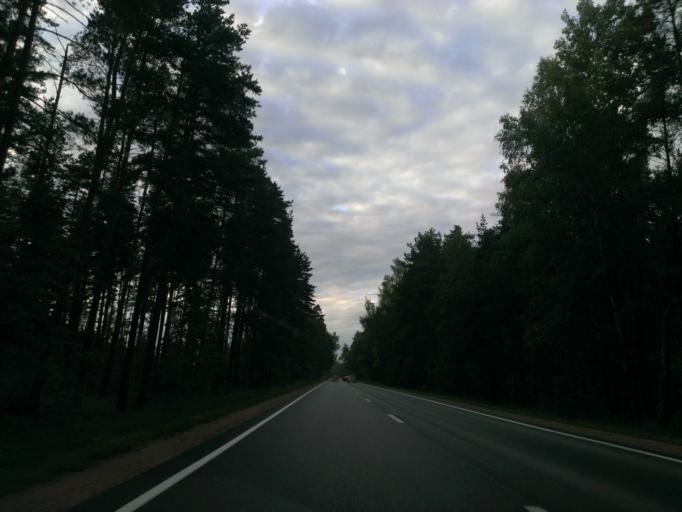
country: LV
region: Salaspils
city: Salaspils
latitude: 56.9454
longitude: 24.3811
